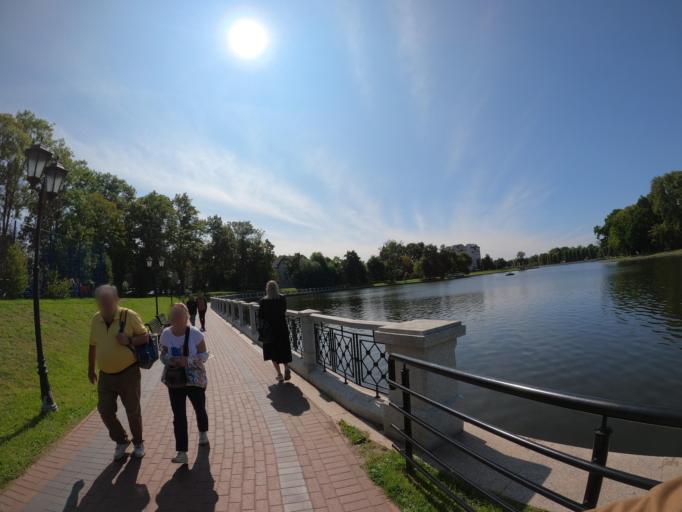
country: RU
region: Kaliningrad
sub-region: Gorod Kaliningrad
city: Kaliningrad
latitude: 54.7301
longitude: 20.5244
